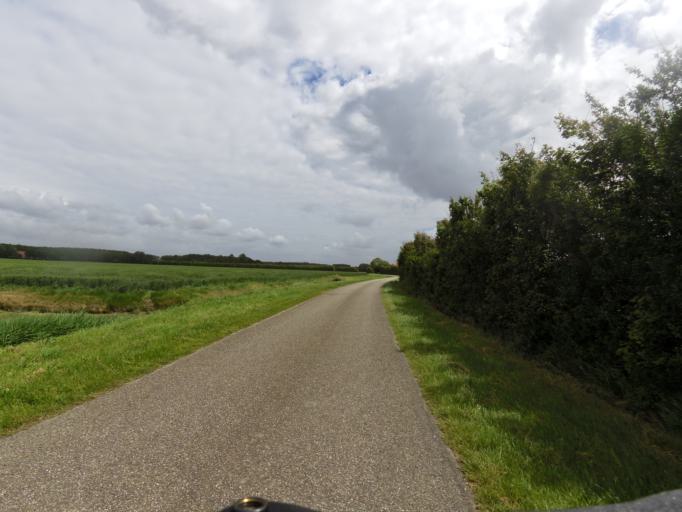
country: NL
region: Zeeland
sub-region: Gemeente Goes
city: Goes
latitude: 51.6231
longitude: 3.9569
